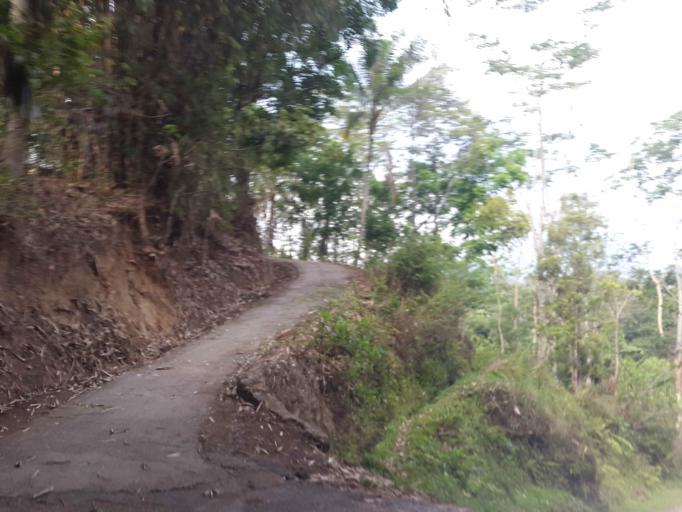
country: ID
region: Central Java
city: Jaten
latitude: -7.6716
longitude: 111.0494
